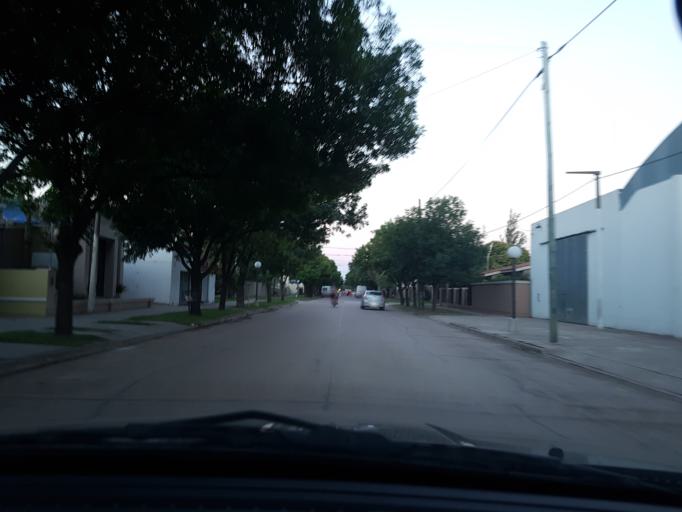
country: AR
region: Cordoba
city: General Cabrera
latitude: -32.7600
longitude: -63.7975
